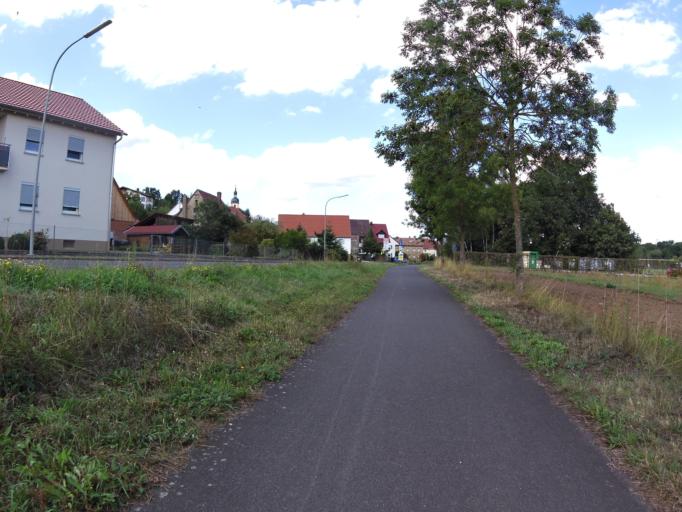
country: DE
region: Bavaria
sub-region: Regierungsbezirk Unterfranken
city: Grafenrheinfeld
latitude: 49.9714
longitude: 10.1729
